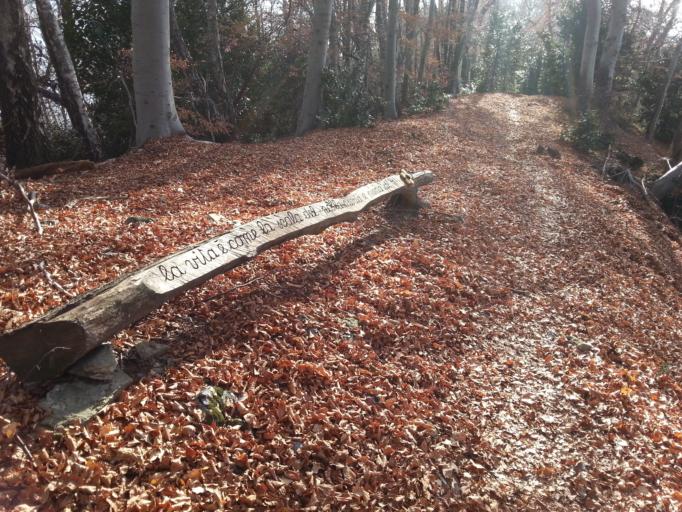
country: IT
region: Lombardy
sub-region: Provincia di Como
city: Maslianico
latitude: 45.8570
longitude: 9.0507
